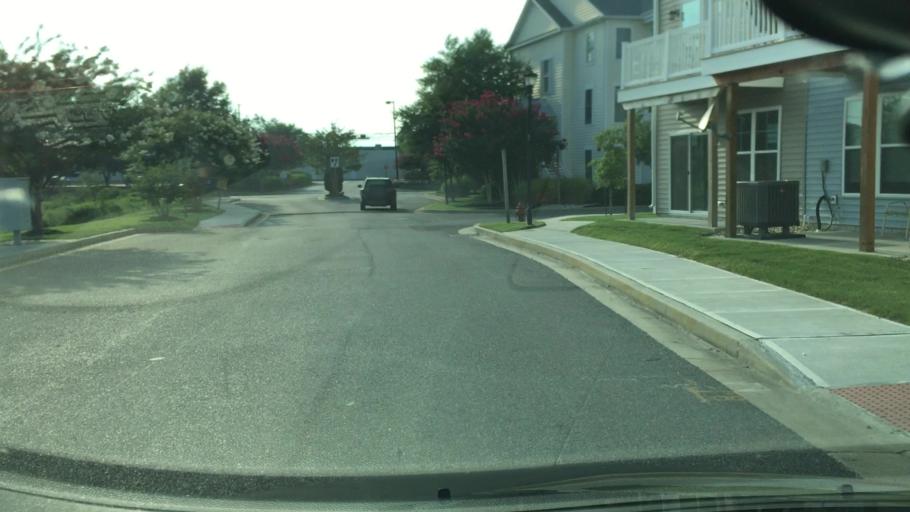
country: US
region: Maryland
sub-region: Worcester County
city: West Ocean City
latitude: 38.3377
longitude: -75.1036
